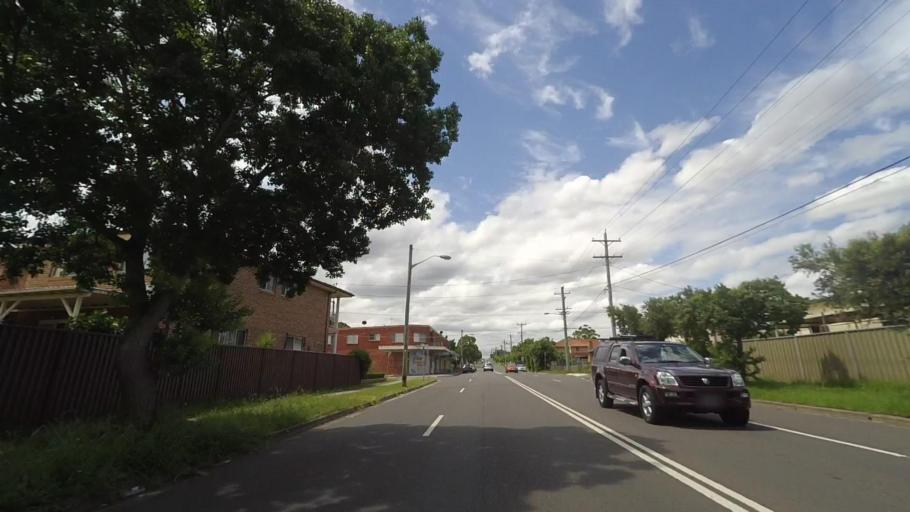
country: AU
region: New South Wales
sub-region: Fairfield
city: Fairfield Heights
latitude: -33.8792
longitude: 150.9414
